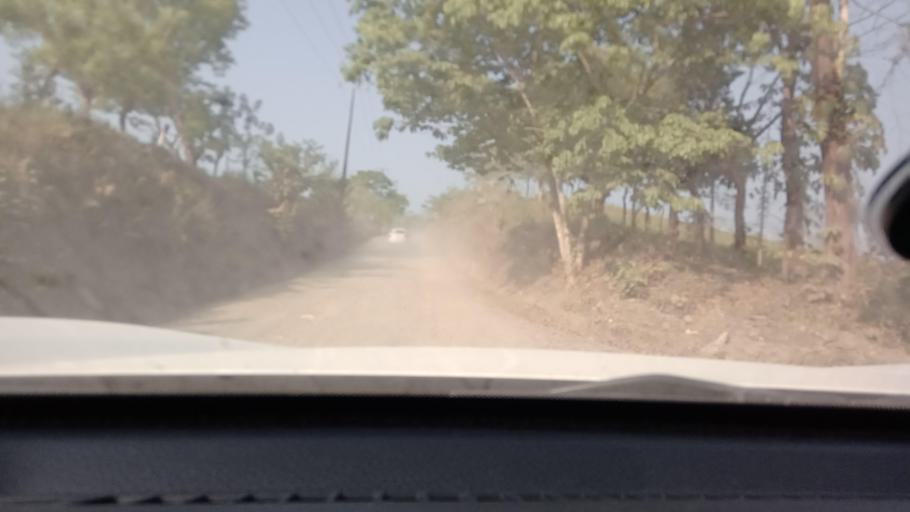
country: MX
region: Tabasco
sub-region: Huimanguillo
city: Francisco Rueda
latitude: 17.6488
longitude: -93.9044
